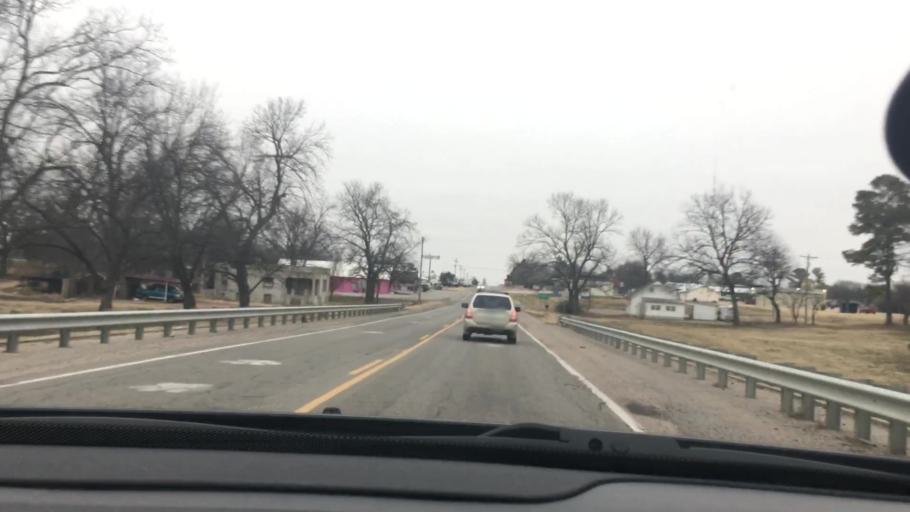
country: US
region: Oklahoma
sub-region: Garvin County
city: Stratford
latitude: 34.7941
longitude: -96.9674
